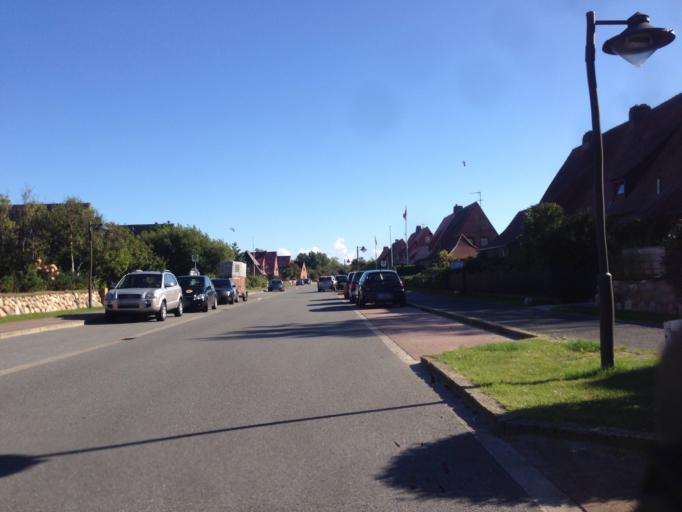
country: DE
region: Schleswig-Holstein
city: List
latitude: 55.0229
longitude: 8.4197
